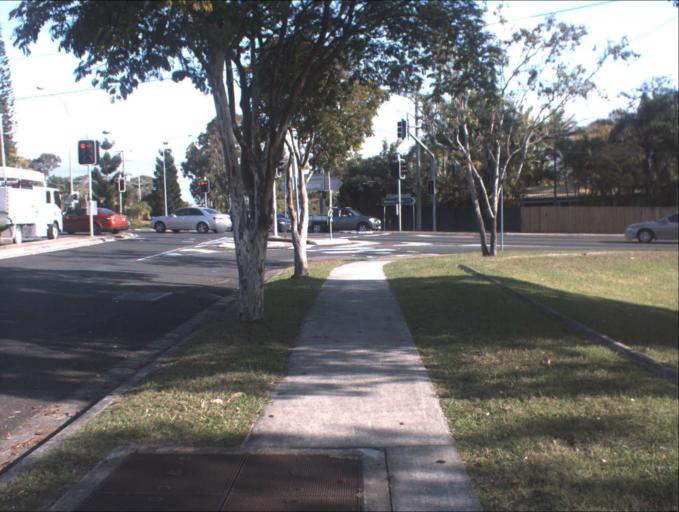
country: AU
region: Queensland
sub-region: Logan
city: Logan Reserve
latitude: -27.6802
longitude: 153.0888
